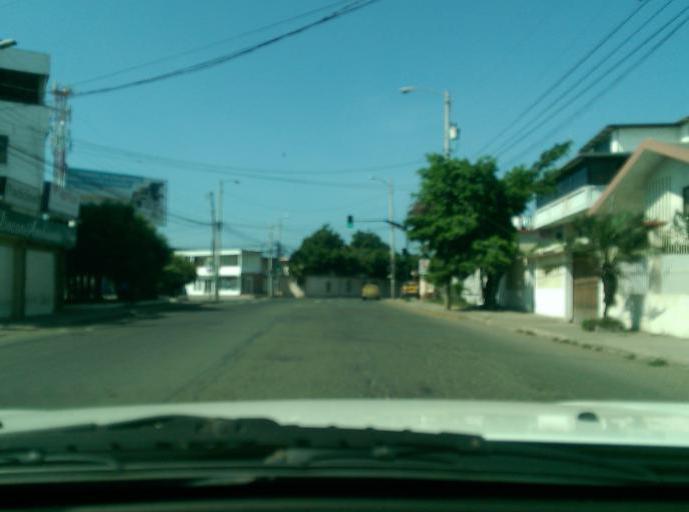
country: EC
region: Manabi
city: Manta
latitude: -0.9458
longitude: -80.7377
